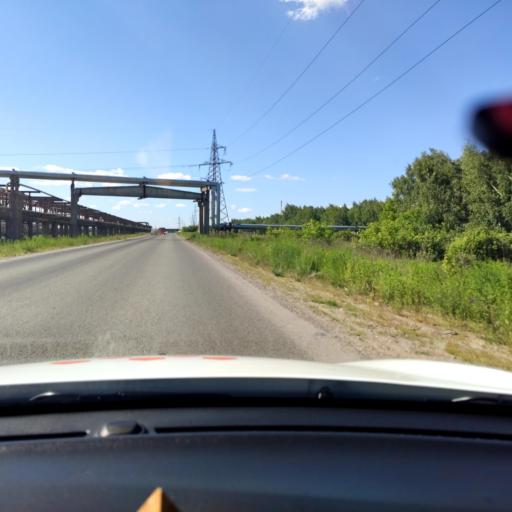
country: RU
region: Tatarstan
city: Staroye Arakchino
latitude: 55.8773
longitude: 48.9758
